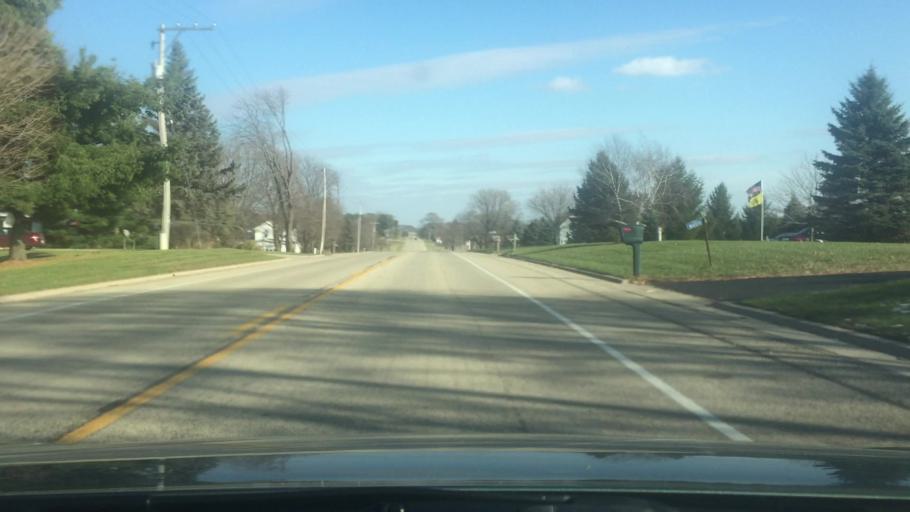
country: US
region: Wisconsin
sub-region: Jefferson County
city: Fort Atkinson
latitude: 42.9391
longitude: -88.7773
